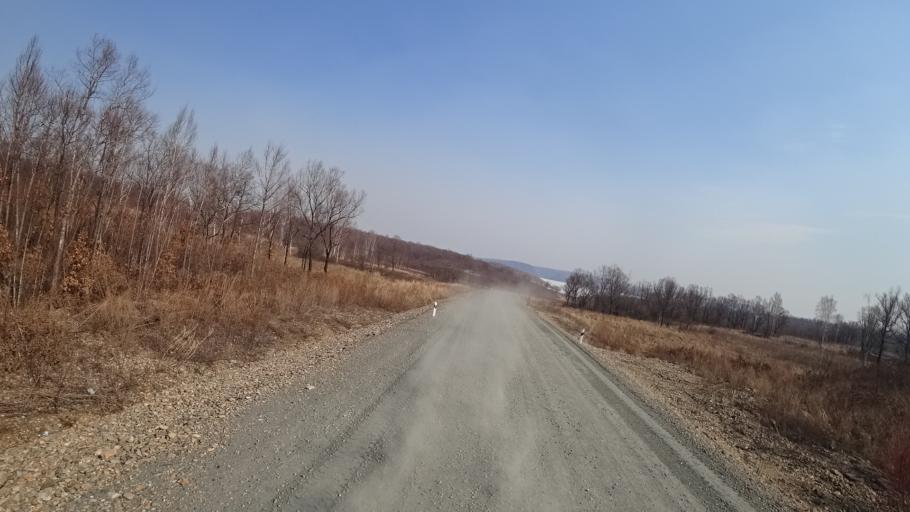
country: RU
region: Amur
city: Novobureyskiy
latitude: 49.8271
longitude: 129.9914
